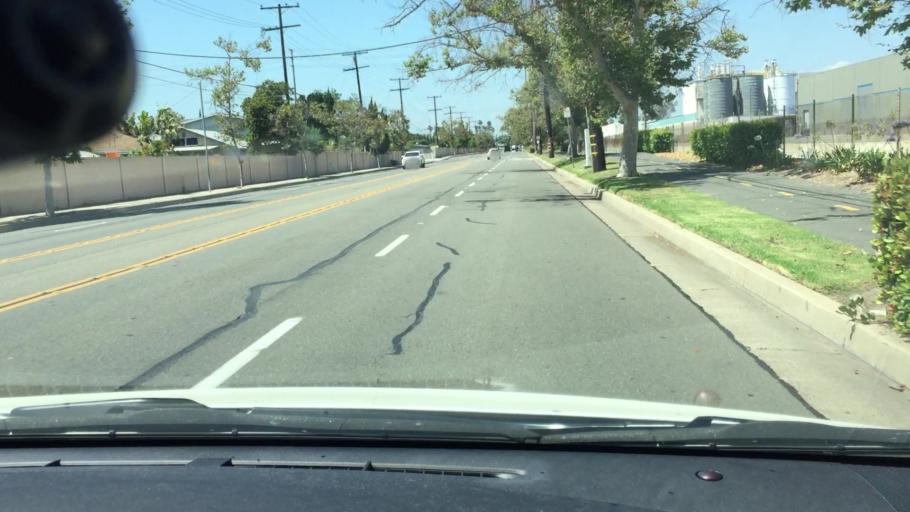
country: US
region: California
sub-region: Orange County
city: Santa Ana
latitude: 33.7110
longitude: -117.8768
